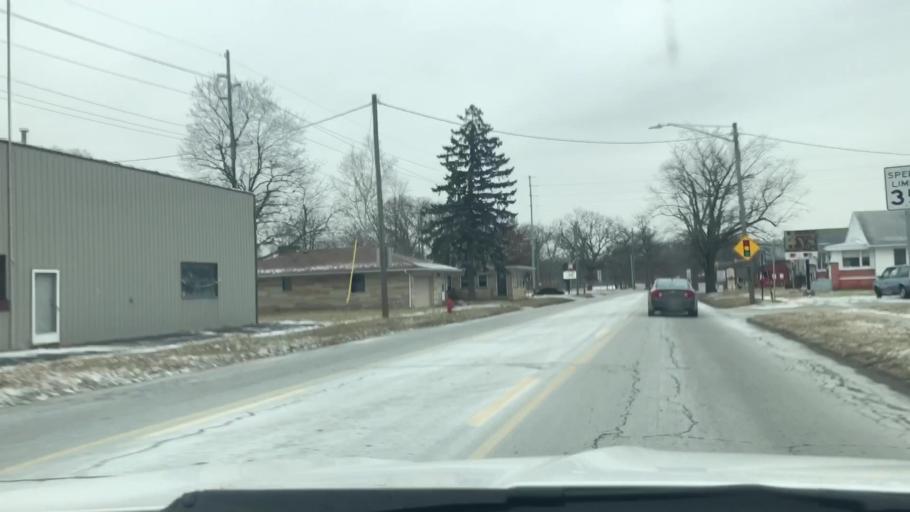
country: US
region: Indiana
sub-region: Fulton County
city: Rochester
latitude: 41.0645
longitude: -86.2080
